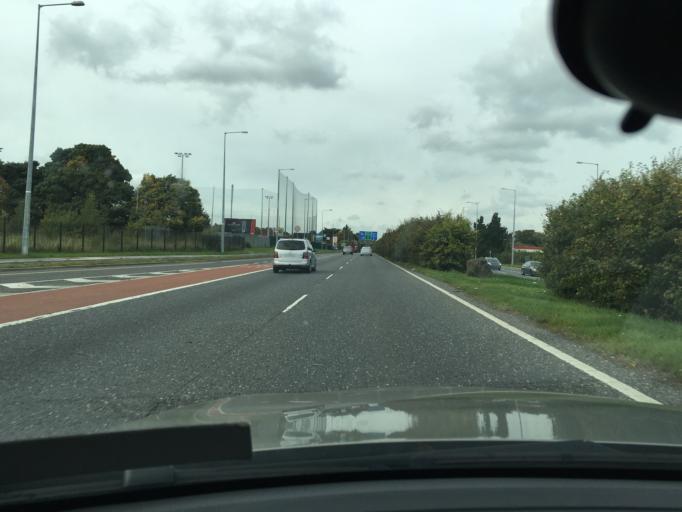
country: IE
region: Leinster
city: Castleknock
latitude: 53.3771
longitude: -6.3475
